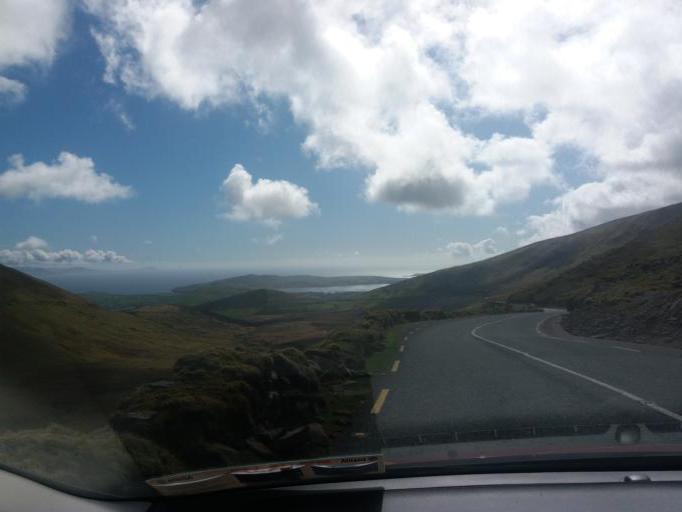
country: IE
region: Munster
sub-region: Ciarrai
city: Dingle
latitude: 52.1802
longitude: -10.2131
